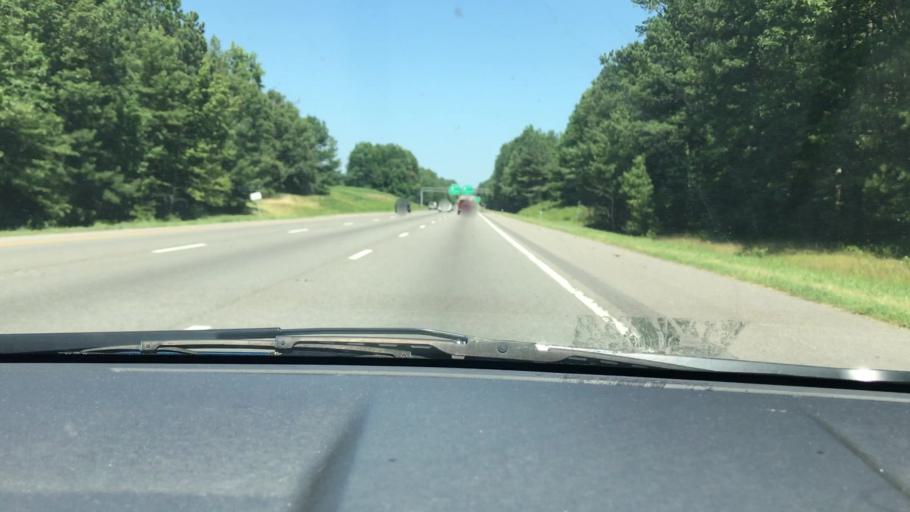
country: US
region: Virginia
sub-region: Henrico County
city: Glen Allen
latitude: 37.6778
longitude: -77.5555
